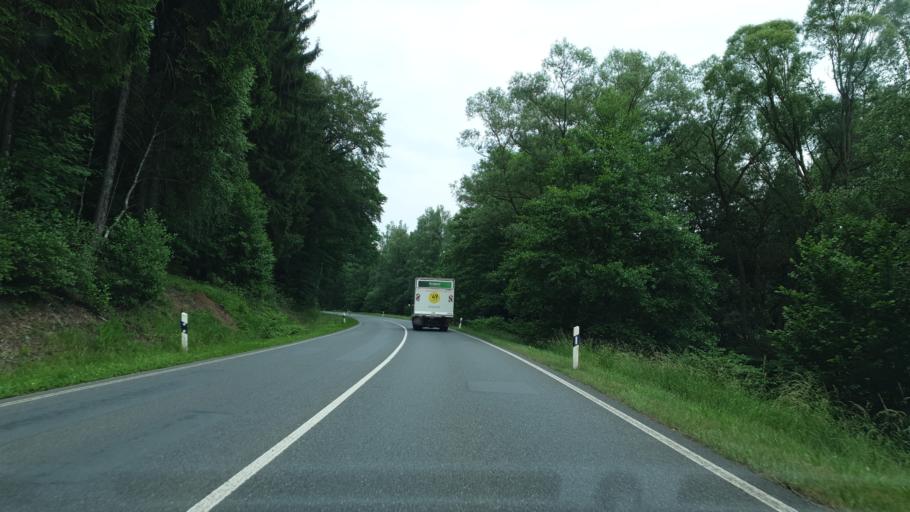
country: DE
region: Saxony
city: Lengenfeld
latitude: 50.5516
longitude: 12.3844
